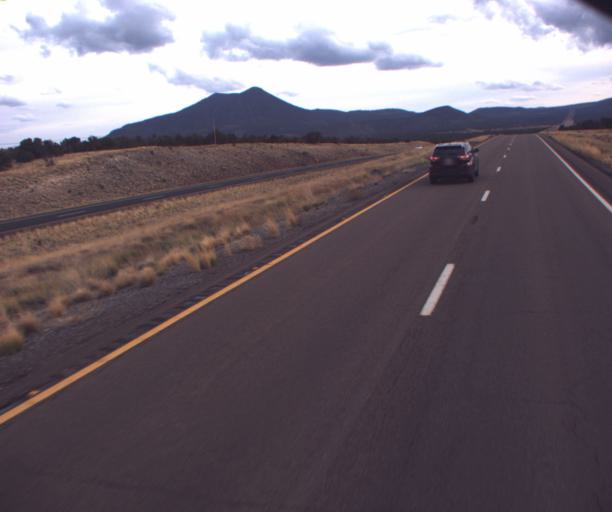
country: US
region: Arizona
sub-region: Coconino County
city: Flagstaff
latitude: 35.4725
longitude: -111.5580
